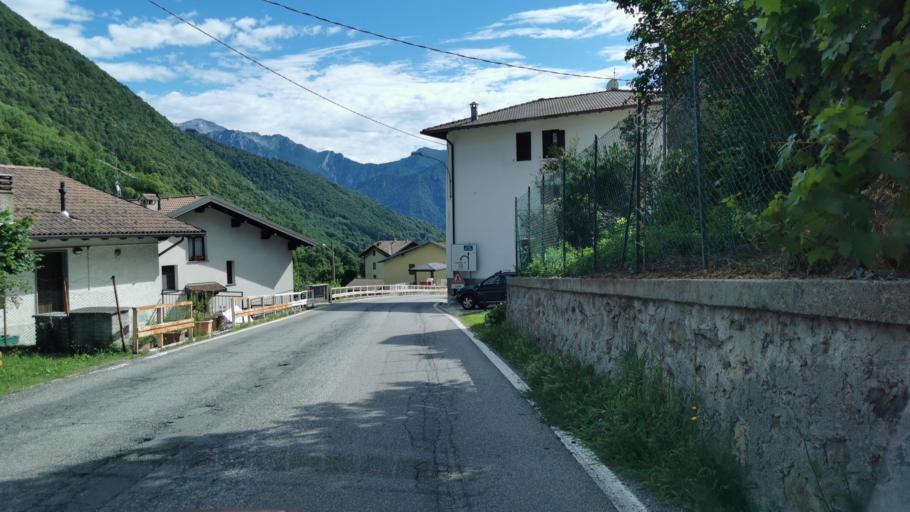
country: IT
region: Lombardy
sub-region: Provincia di Lecco
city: Casargo
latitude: 46.0452
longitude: 9.3917
